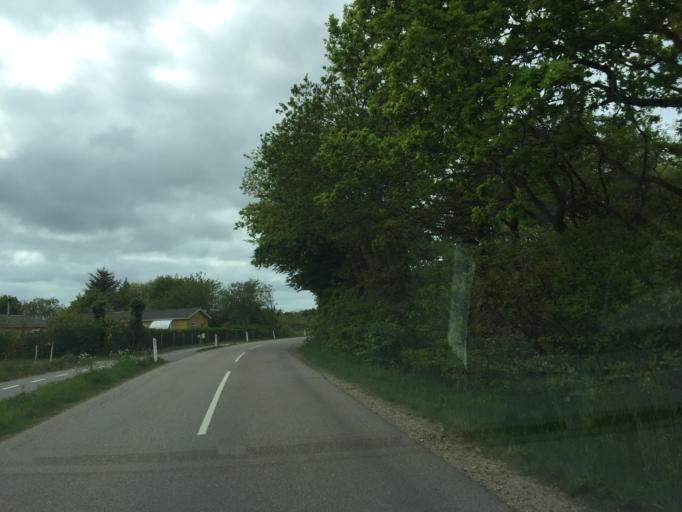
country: DK
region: Central Jutland
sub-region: Ringkobing-Skjern Kommune
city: Ringkobing
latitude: 55.9976
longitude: 8.3257
